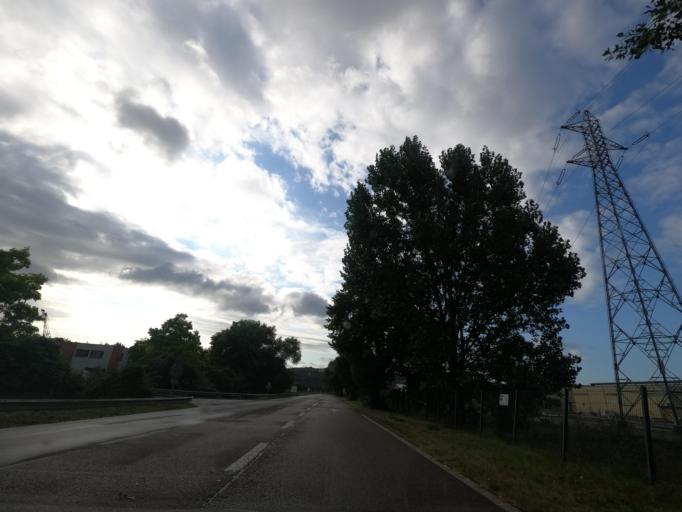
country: FR
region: Haute-Normandie
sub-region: Departement de la Seine-Maritime
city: Grand-Couronne
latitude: 49.3685
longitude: 1.0079
